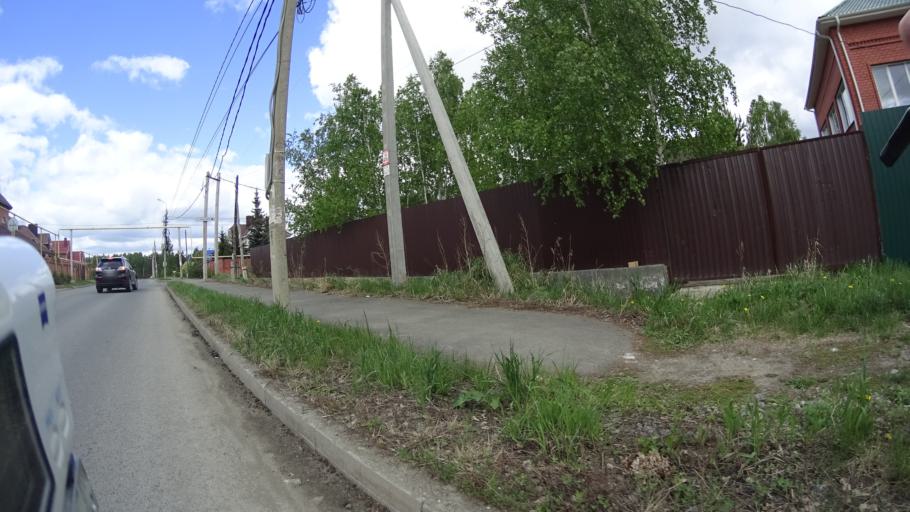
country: RU
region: Chelyabinsk
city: Sargazy
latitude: 55.1591
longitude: 61.2519
